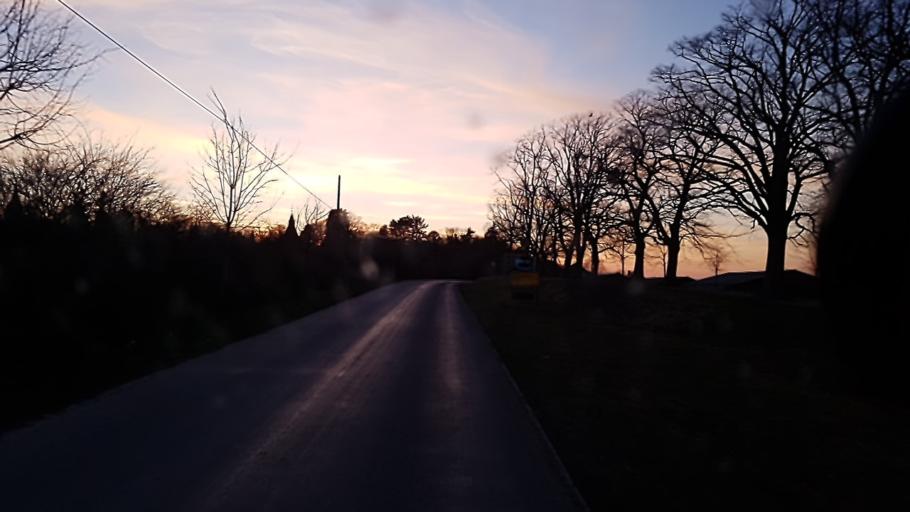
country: BE
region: Wallonia
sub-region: Province du Luxembourg
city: Wellin
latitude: 50.0709
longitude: 5.0753
